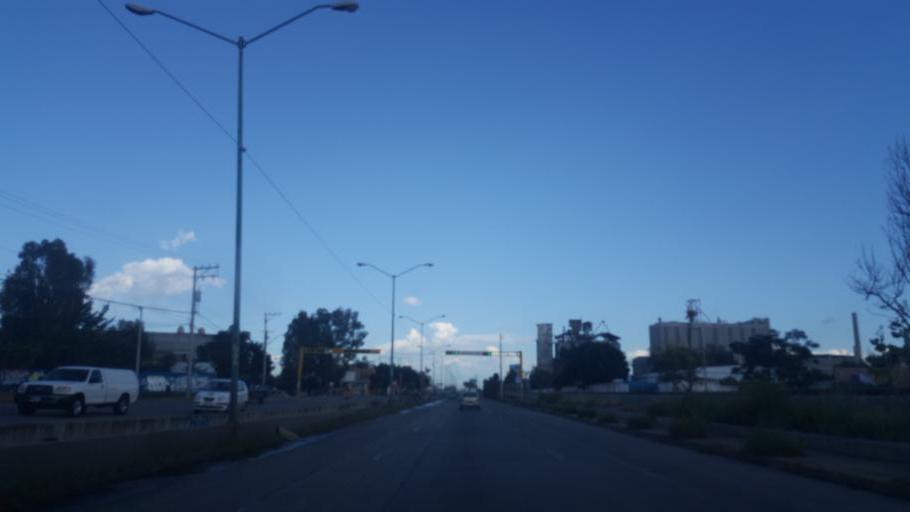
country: MX
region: Guanajuato
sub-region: Leon
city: San Jose de Duran (Los Troncoso)
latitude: 21.0867
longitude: -101.6703
